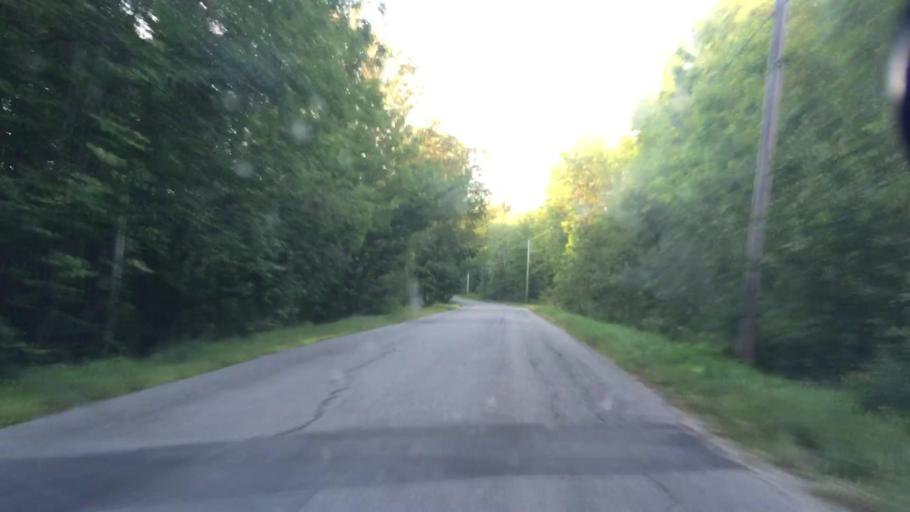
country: US
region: Maine
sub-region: Waldo County
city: Frankfort
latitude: 44.6685
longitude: -68.9259
